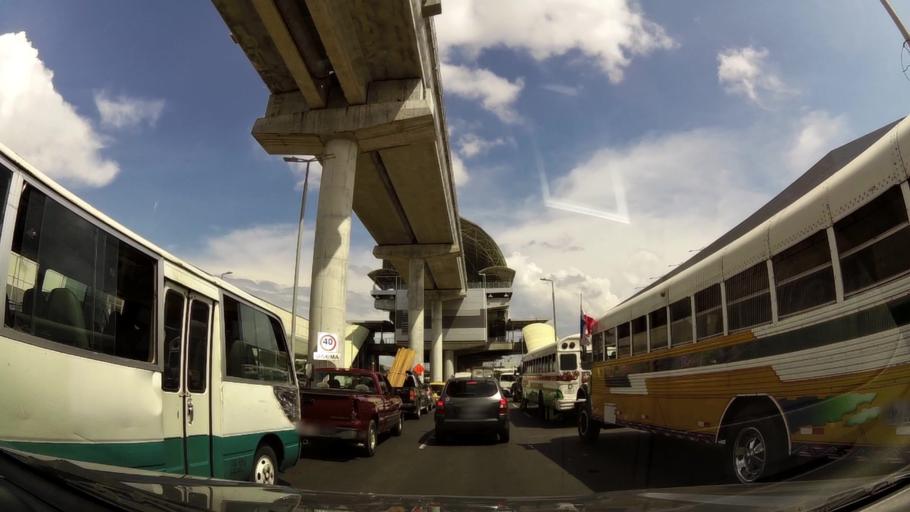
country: PA
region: Panama
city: Panama
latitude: 9.0290
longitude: -79.5069
